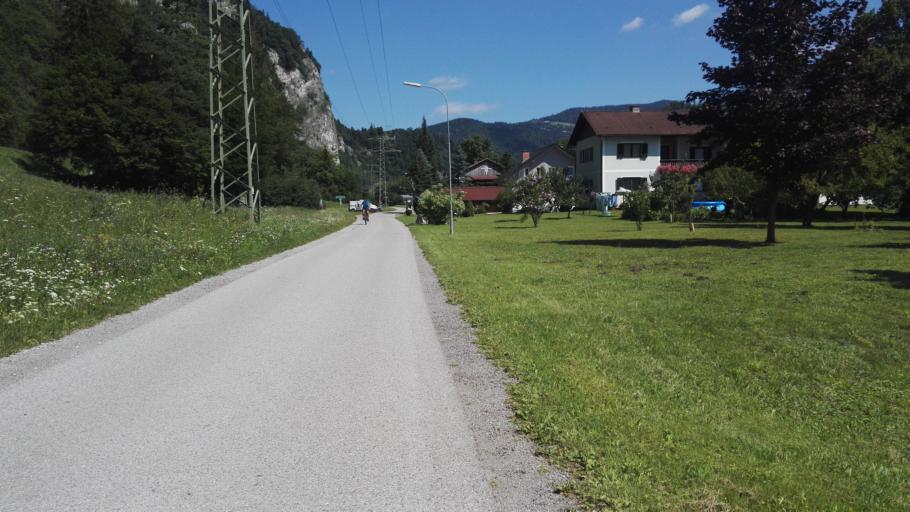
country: AT
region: Styria
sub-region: Politischer Bezirk Graz-Umgebung
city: Peggau
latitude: 47.2113
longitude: 15.3358
